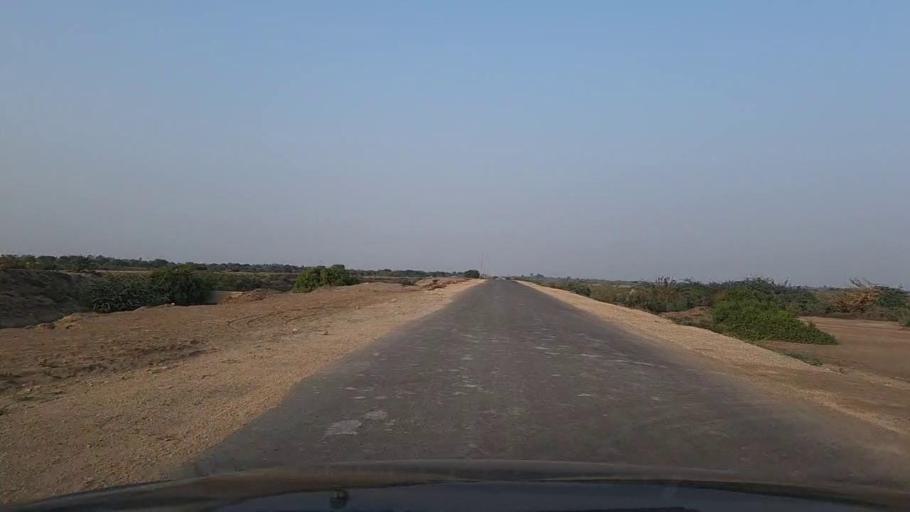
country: PK
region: Sindh
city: Mirpur Sakro
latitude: 24.4664
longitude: 67.7981
